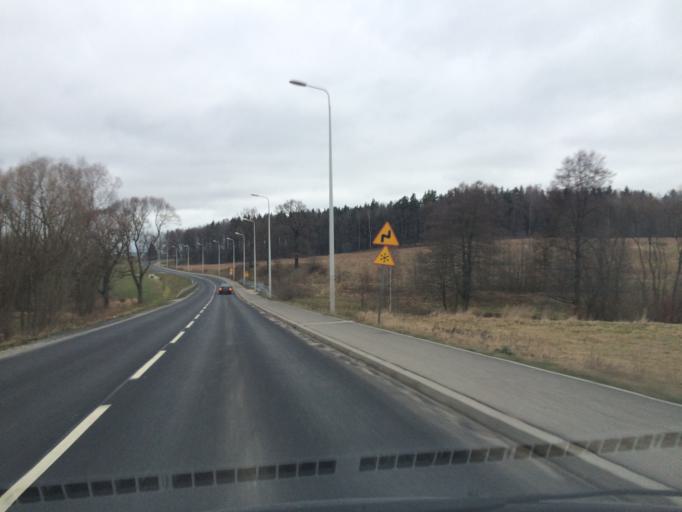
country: PL
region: Lower Silesian Voivodeship
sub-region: Powiat lubanski
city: Luban
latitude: 51.1334
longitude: 15.2752
